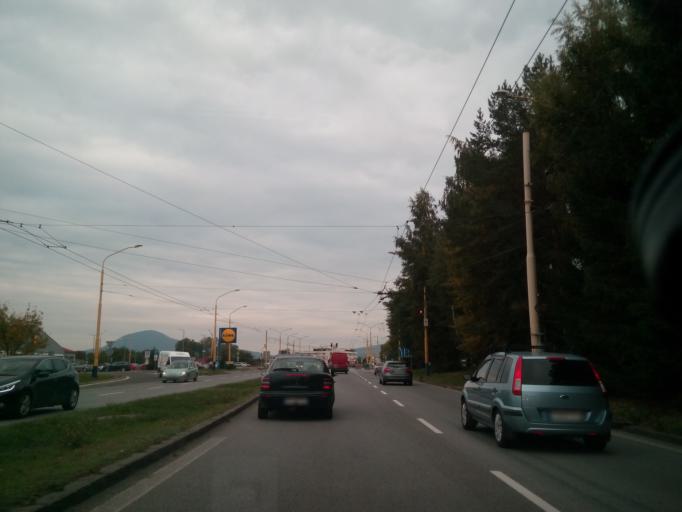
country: SK
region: Presovsky
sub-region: Okres Presov
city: Presov
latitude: 48.9892
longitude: 21.2653
